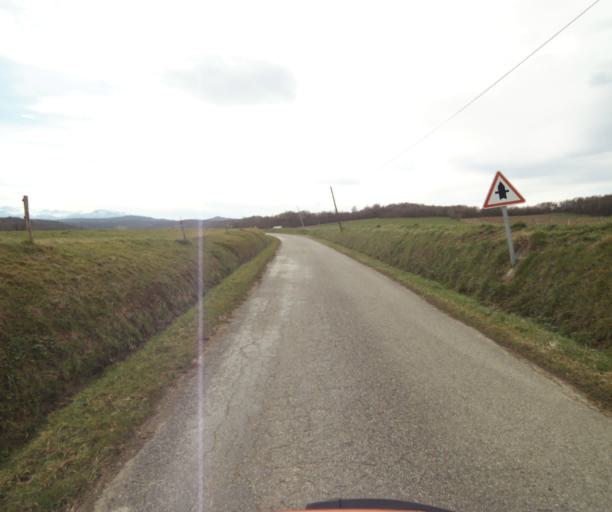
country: FR
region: Midi-Pyrenees
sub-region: Departement de l'Ariege
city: Verniolle
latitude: 43.0821
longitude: 1.7109
